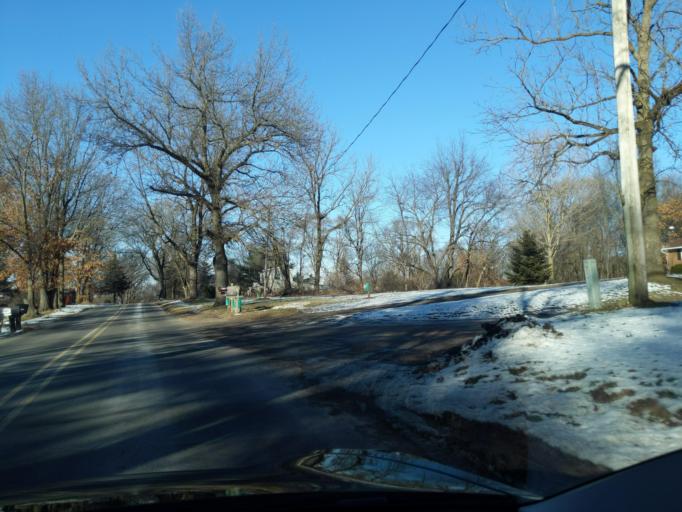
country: US
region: Michigan
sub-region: Ingham County
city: Stockbridge
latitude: 42.4263
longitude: -84.1512
